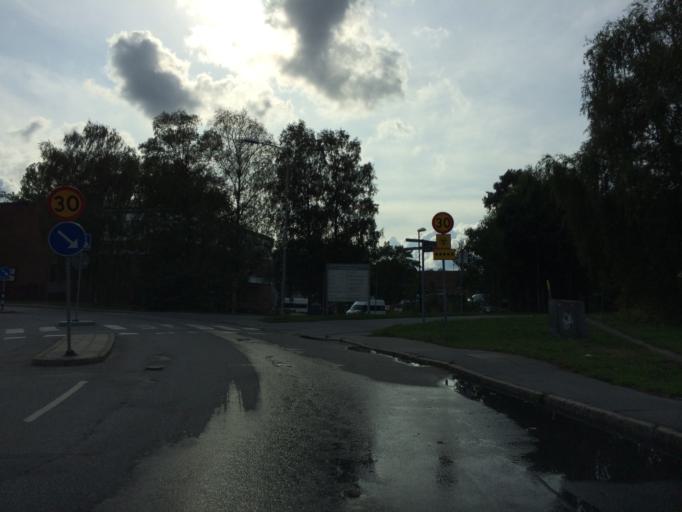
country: SE
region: Stockholm
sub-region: Huddinge Kommun
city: Segeltorp
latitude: 59.2887
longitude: 17.9641
